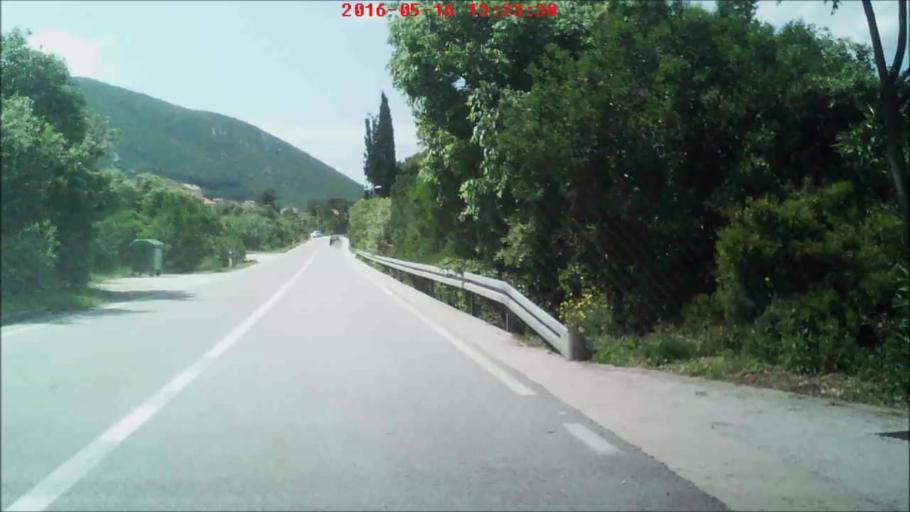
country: HR
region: Dubrovacko-Neretvanska
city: Ston
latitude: 42.8434
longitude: 17.7110
